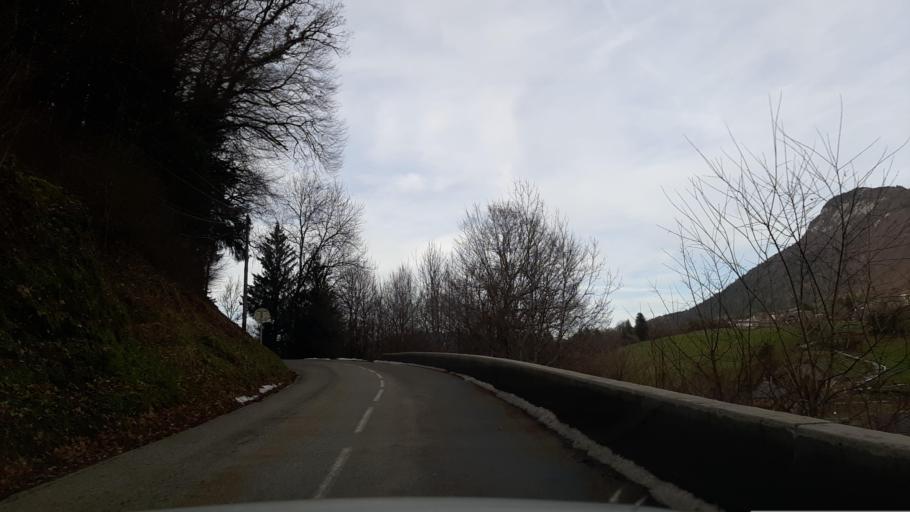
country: FR
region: Rhone-Alpes
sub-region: Departement de la Haute-Savoie
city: Doussard
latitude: 45.6780
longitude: 6.1331
